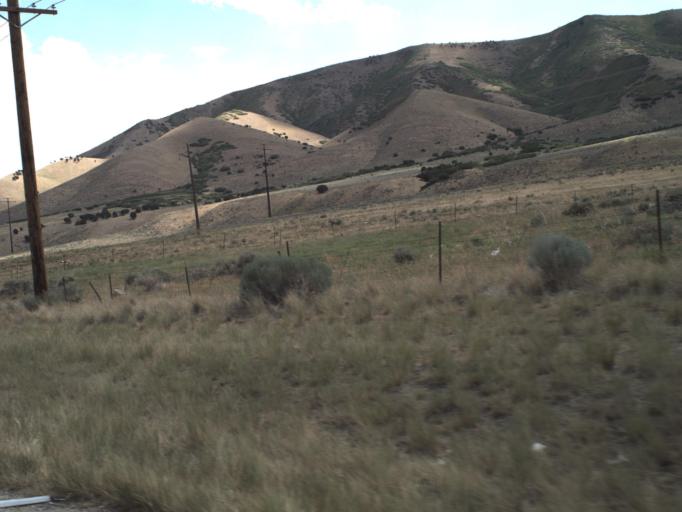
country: US
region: Utah
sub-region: Tooele County
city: Tooele
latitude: 40.4911
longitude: -112.3336
